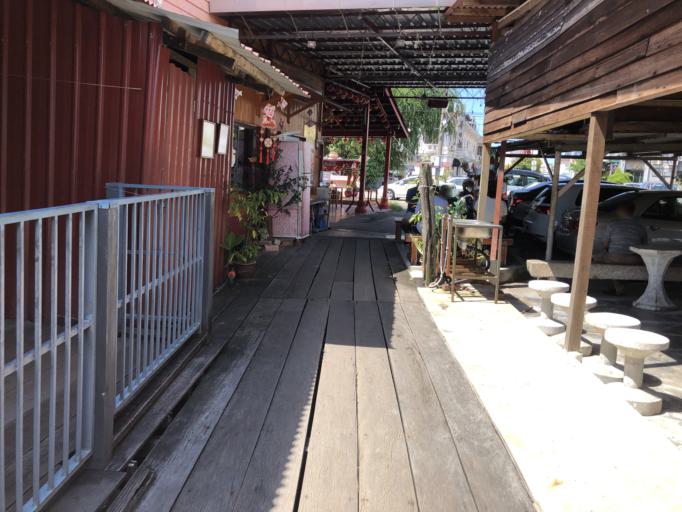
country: MY
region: Penang
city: George Town
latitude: 5.4132
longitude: 100.3412
